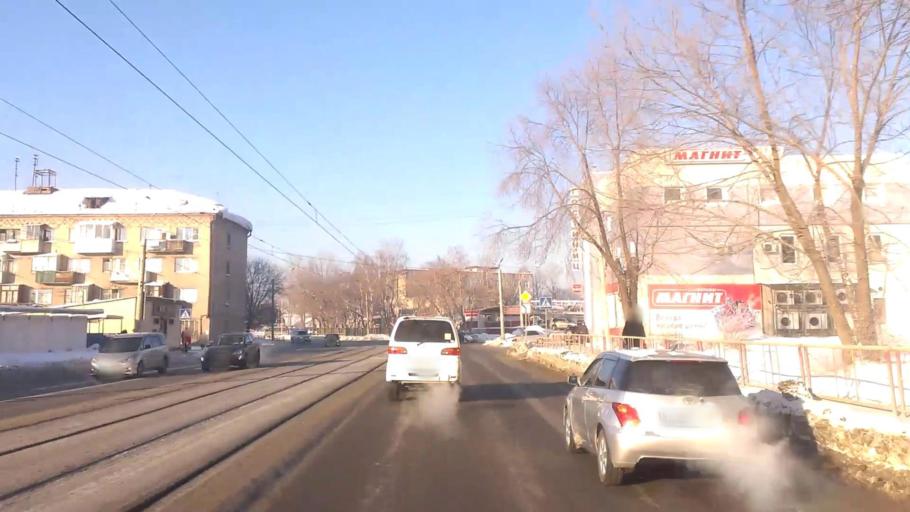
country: RU
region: Altai Krai
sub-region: Gorod Barnaulskiy
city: Barnaul
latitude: 53.3480
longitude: 83.7303
